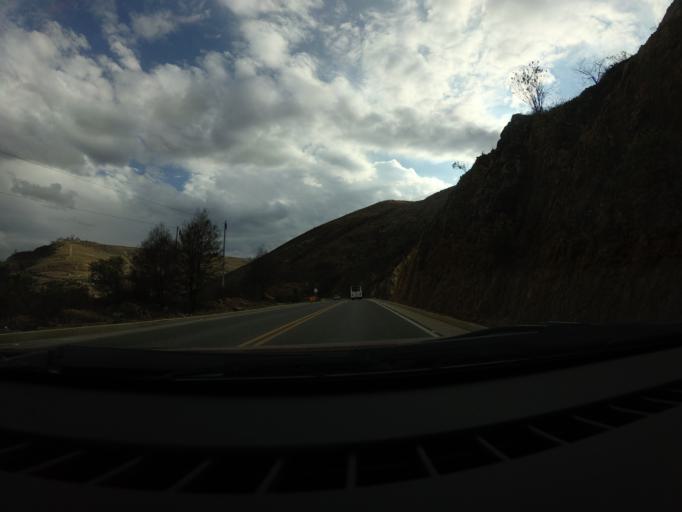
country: CO
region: Boyaca
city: Sachica
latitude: 5.5615
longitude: -73.5015
